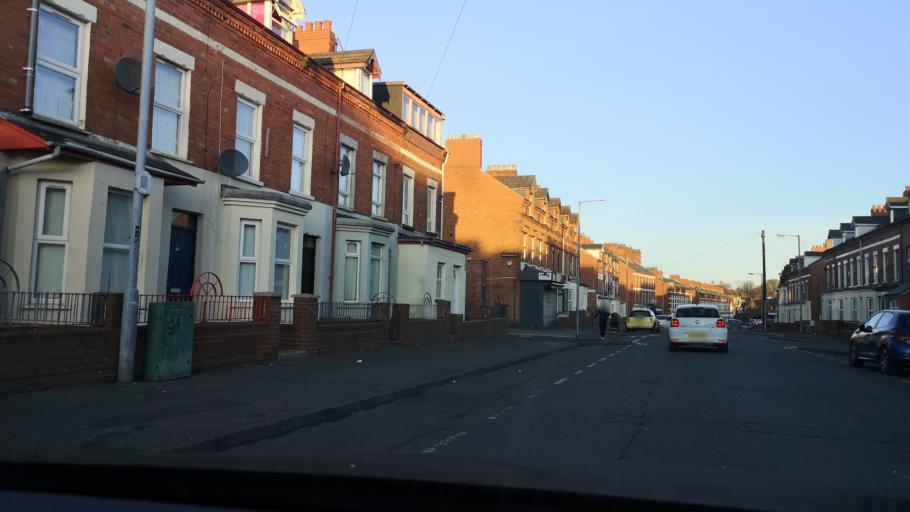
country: GB
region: Northern Ireland
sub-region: City of Belfast
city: Belfast
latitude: 54.5830
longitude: -5.9264
